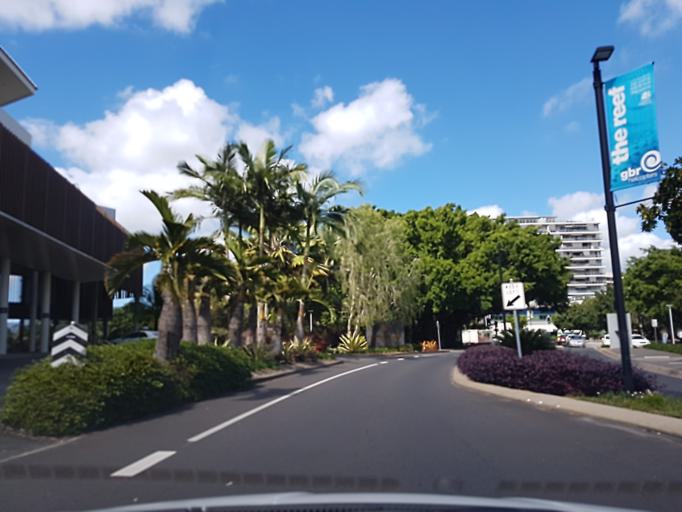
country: AU
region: Queensland
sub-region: Cairns
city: Cairns
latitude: -16.9202
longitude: 145.7799
